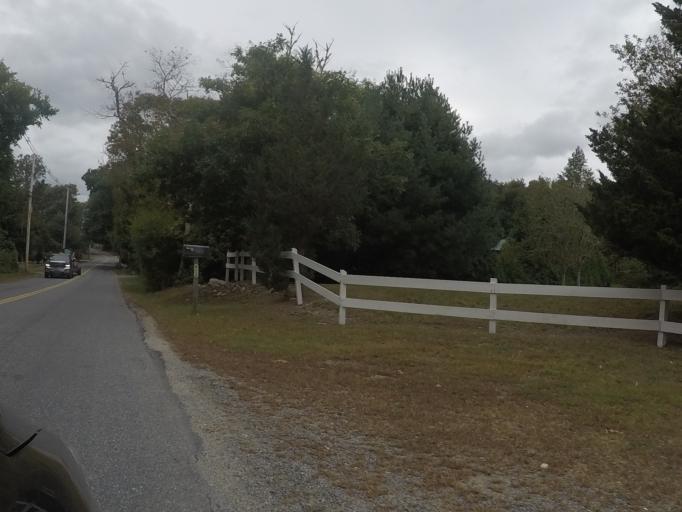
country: US
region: Massachusetts
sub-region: Bristol County
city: Head of Westport
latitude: 41.5595
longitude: -71.0091
